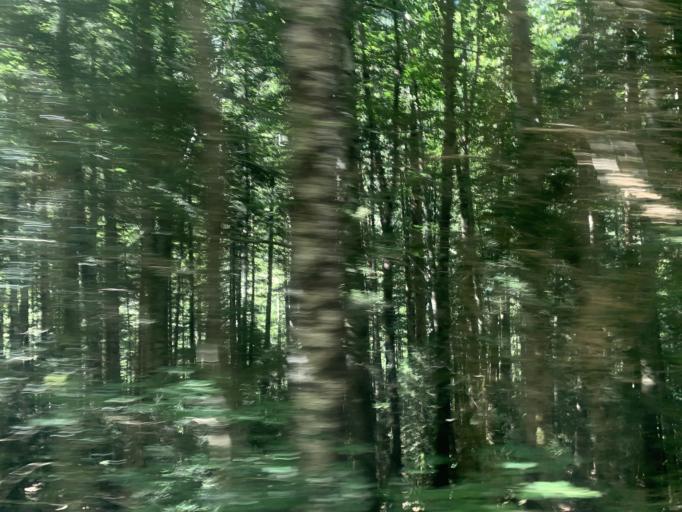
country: ES
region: Aragon
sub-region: Provincia de Huesca
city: Broto
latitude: 42.6519
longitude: -0.0728
